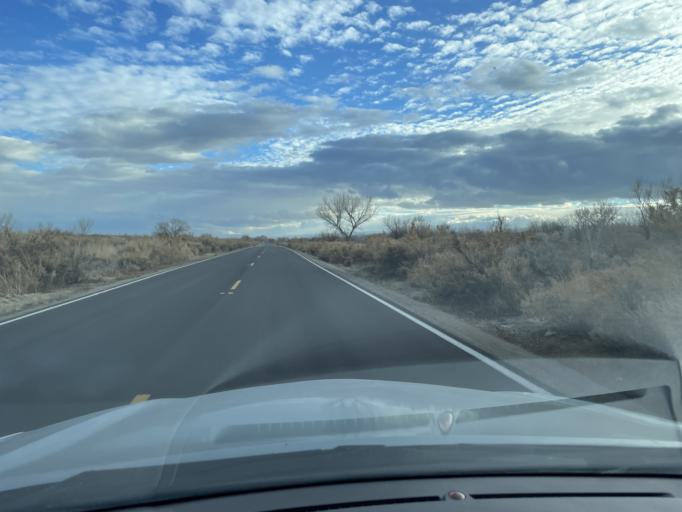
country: US
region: Colorado
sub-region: Montrose County
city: Olathe
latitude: 38.6483
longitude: -107.9950
